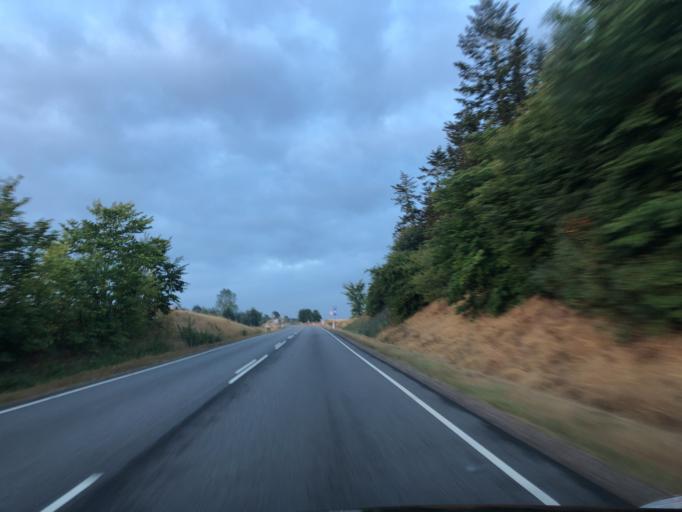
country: DK
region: Zealand
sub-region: Soro Kommune
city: Stenlille
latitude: 55.5227
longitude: 11.5819
